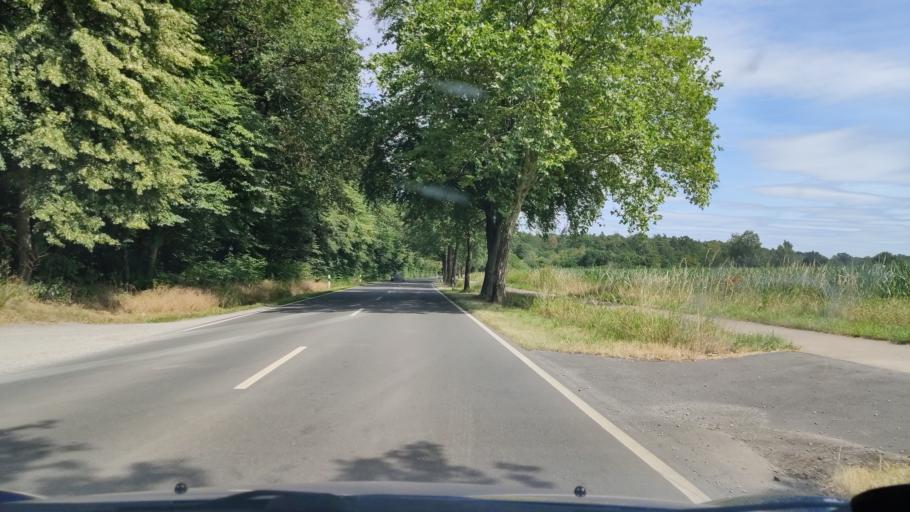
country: DE
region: Lower Saxony
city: Neustadt am Rubenberge
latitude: 52.5509
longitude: 9.4779
